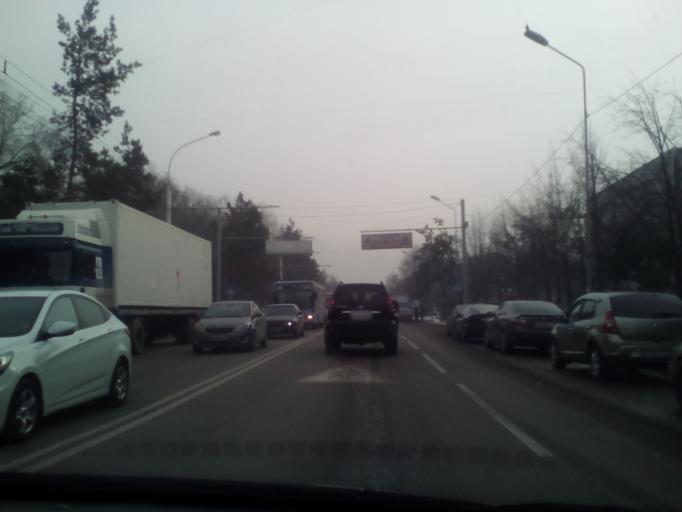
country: KZ
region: Almaty Qalasy
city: Almaty
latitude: 43.2380
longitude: 76.8299
